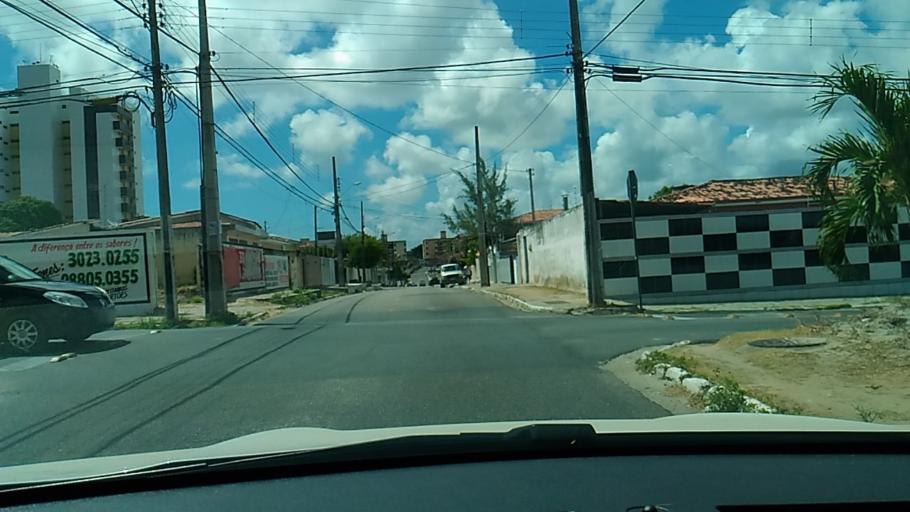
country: BR
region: Paraiba
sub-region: Joao Pessoa
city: Joao Pessoa
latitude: -7.1562
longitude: -34.8415
